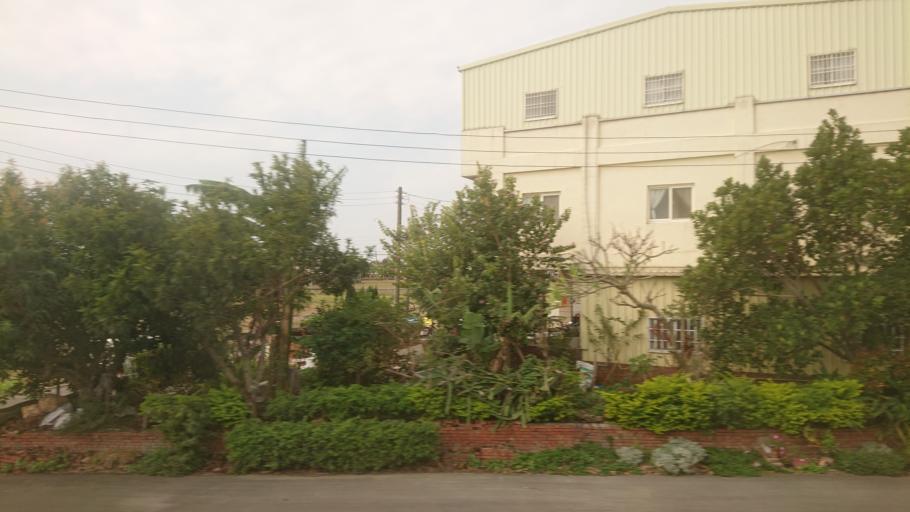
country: TW
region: Taiwan
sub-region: Changhua
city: Chang-hua
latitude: 24.0308
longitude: 120.5346
